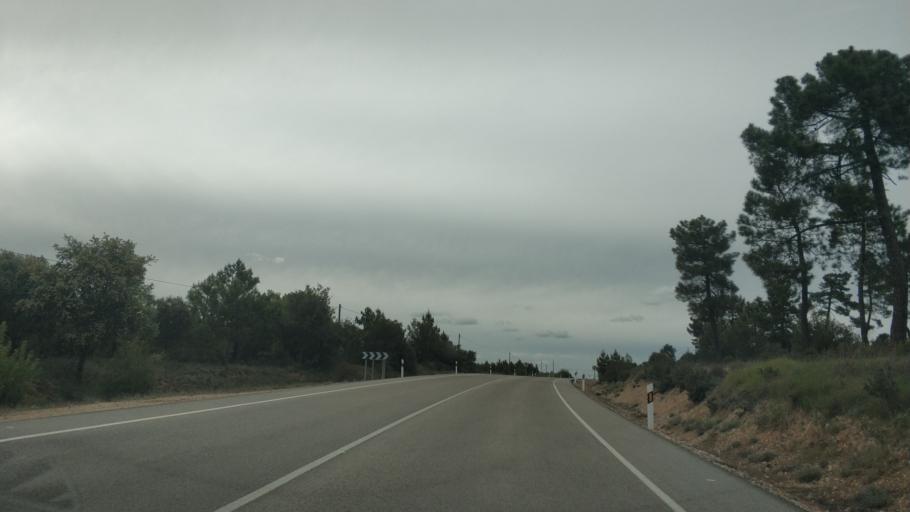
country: ES
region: Castille and Leon
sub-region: Provincia de Soria
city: Quintanas de Gormaz
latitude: 41.5257
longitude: -2.9425
